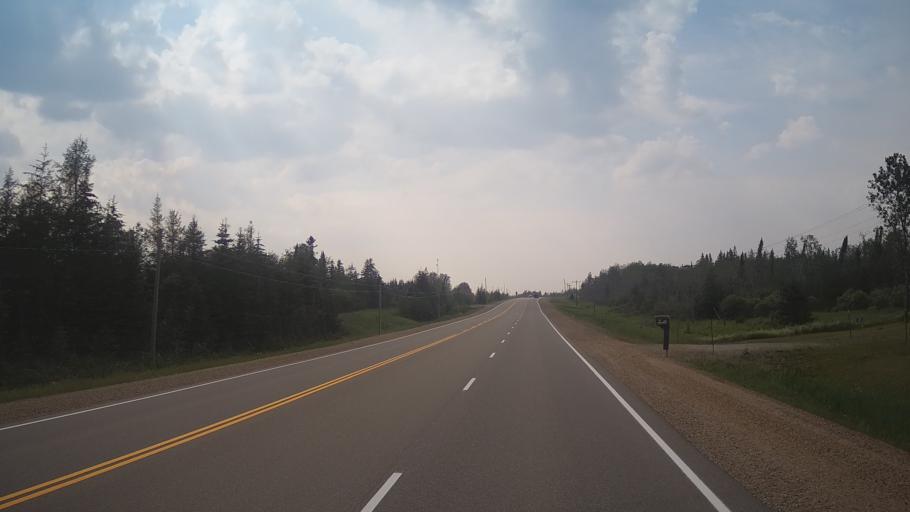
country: CA
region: Ontario
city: Kapuskasing
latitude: 49.4559
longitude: -82.5698
